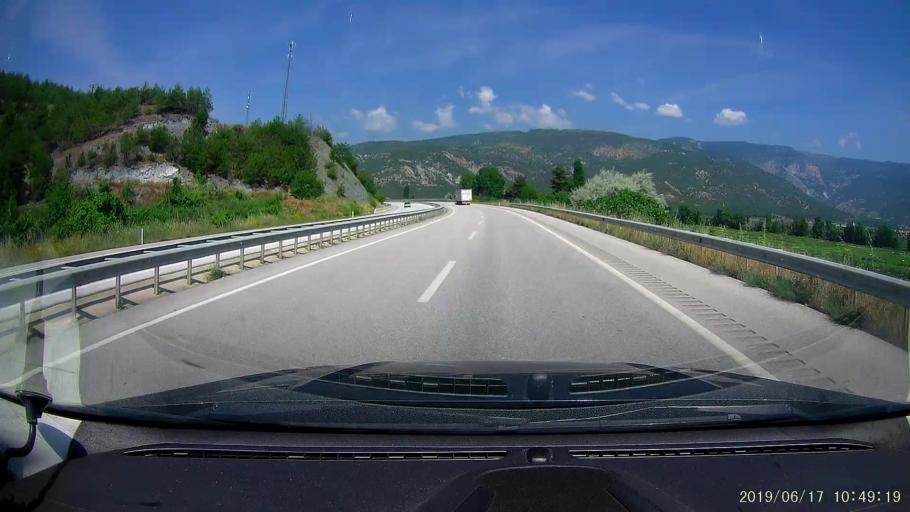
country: TR
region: Corum
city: Hacihamza
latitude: 41.1006
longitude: 34.4127
